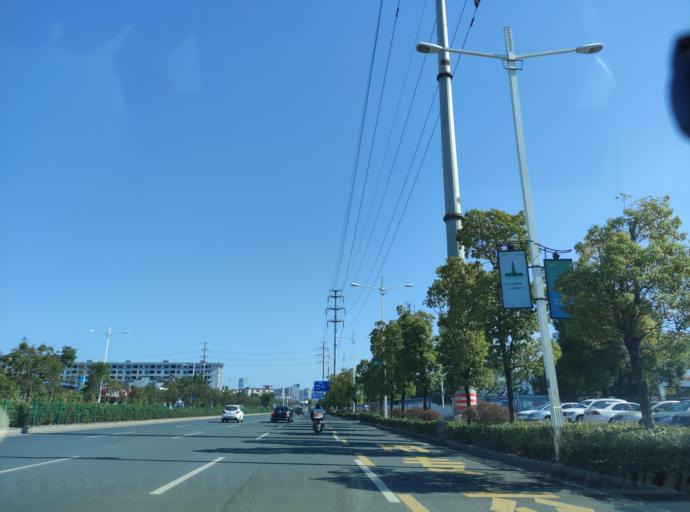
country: CN
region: Jiangxi Sheng
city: Pingxiang
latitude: 27.6570
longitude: 113.8509
